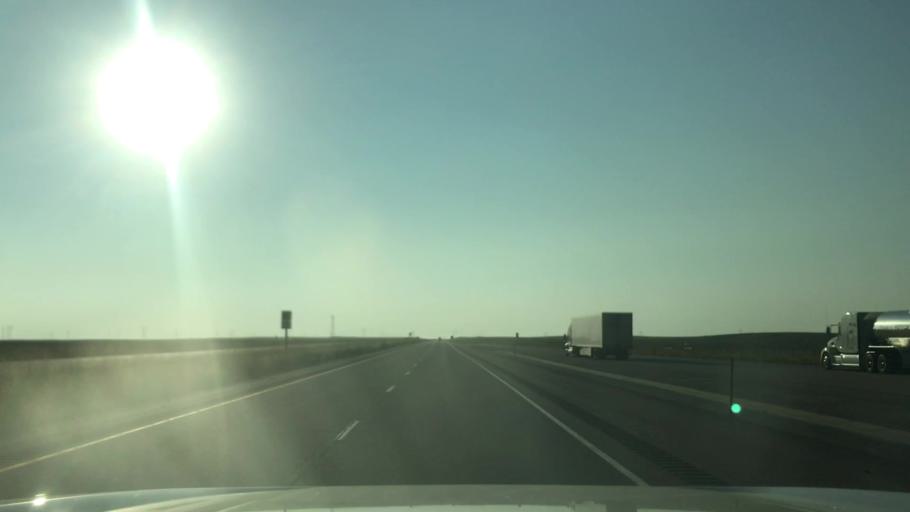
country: US
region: Wyoming
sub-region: Converse County
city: Glenrock
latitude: 42.8003
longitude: -105.6512
